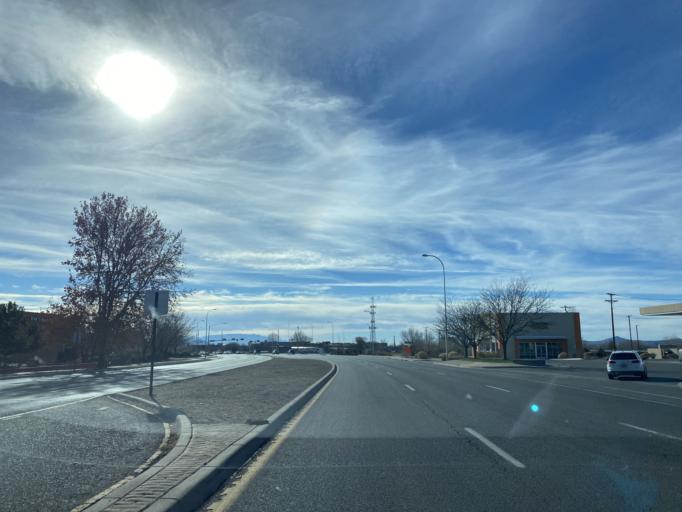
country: US
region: New Mexico
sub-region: Santa Fe County
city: Agua Fria
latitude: 35.6406
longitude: -106.0156
